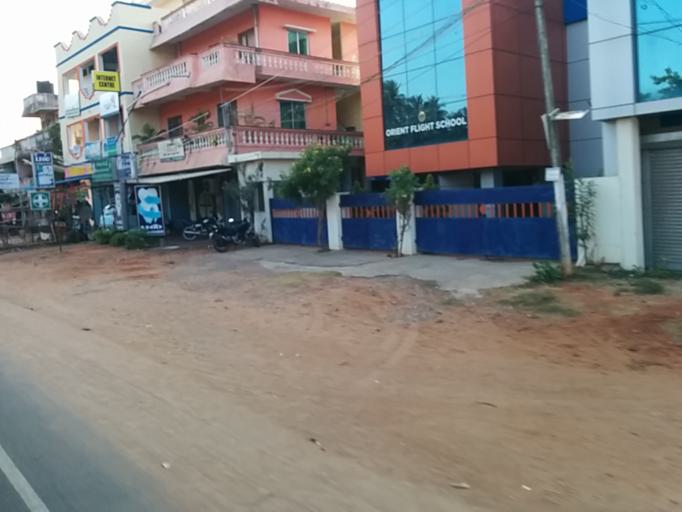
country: IN
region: Tamil Nadu
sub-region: Villupuram
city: Auroville
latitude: 11.9840
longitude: 79.8456
